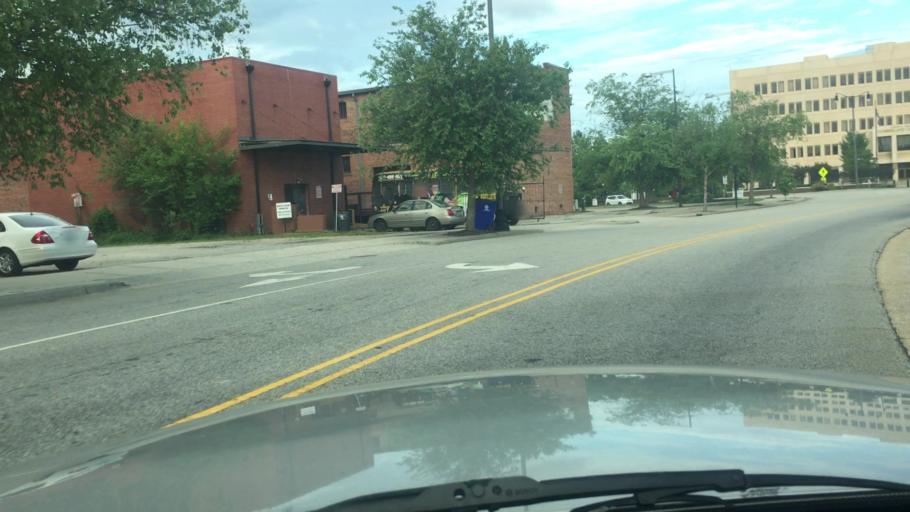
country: US
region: North Carolina
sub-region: Cumberland County
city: Fayetteville
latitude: 35.0517
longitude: -78.8784
